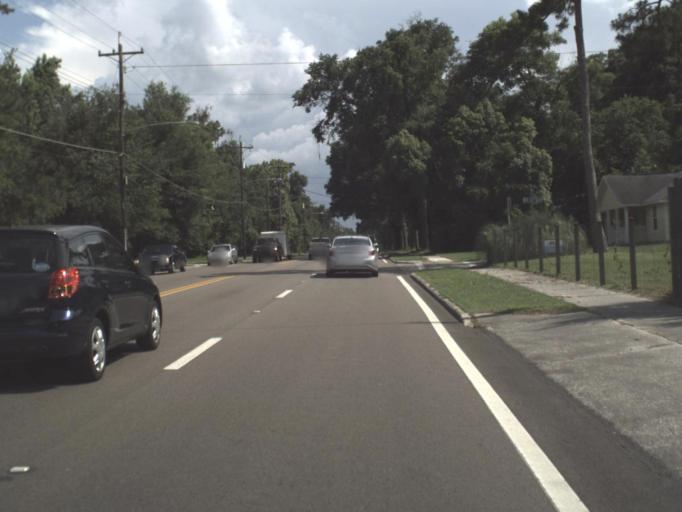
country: US
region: Florida
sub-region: Alachua County
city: Gainesville
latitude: 29.6845
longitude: -82.3308
